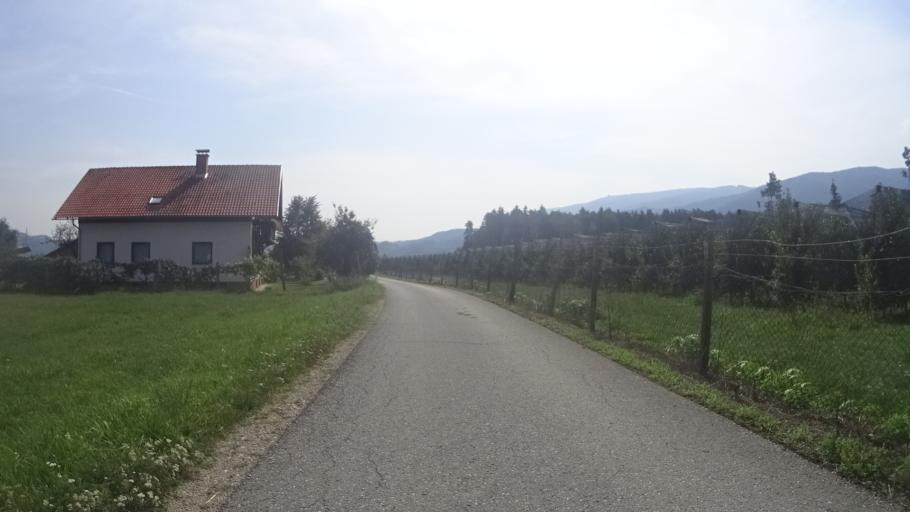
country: SI
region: Selnica ob Dravi
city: Selnica ob Dravi
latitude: 46.5439
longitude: 15.4831
